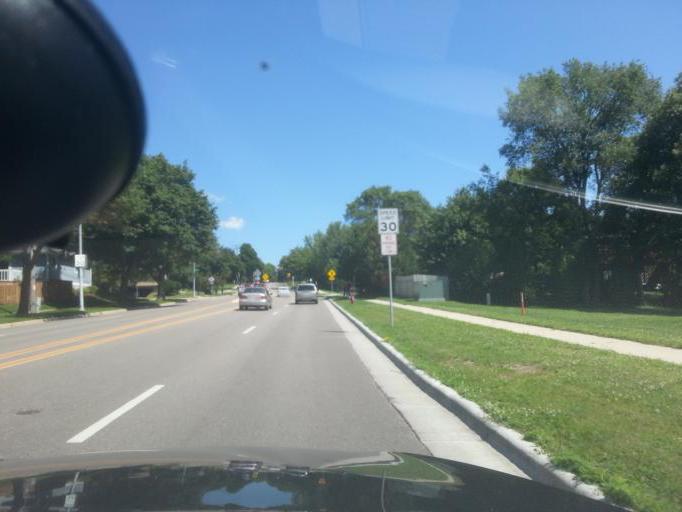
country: US
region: Wisconsin
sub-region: Dane County
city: Middleton
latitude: 43.0676
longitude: -89.5025
